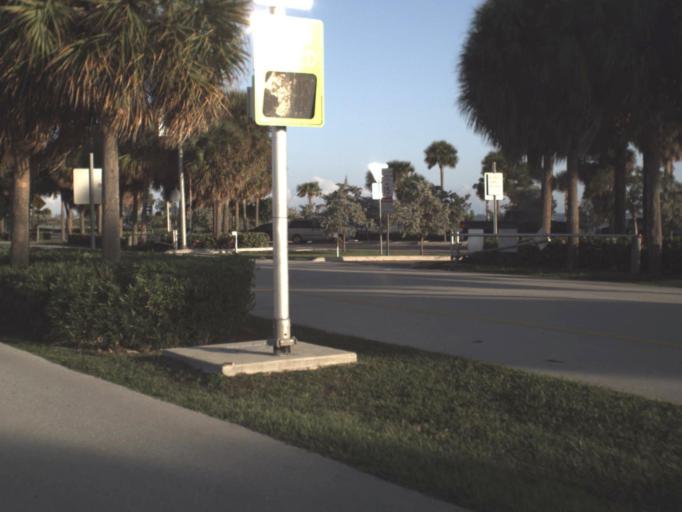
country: US
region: Florida
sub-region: Miami-Dade County
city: Miami
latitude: 25.7462
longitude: -80.1920
